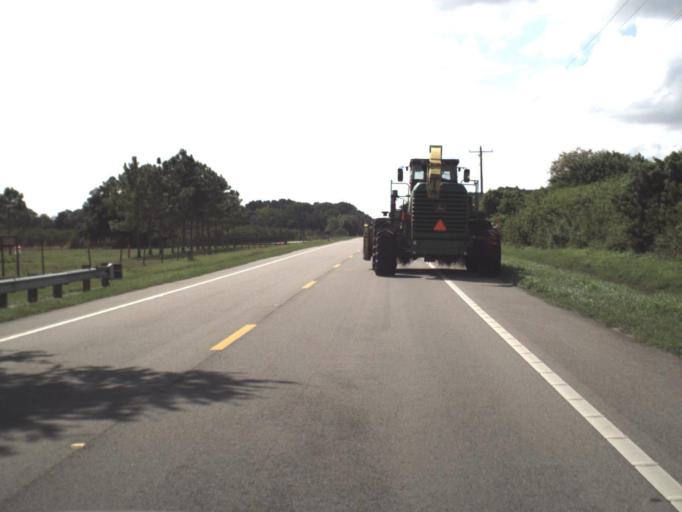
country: US
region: Florida
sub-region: Hillsborough County
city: Wimauma
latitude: 27.4740
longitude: -82.2523
